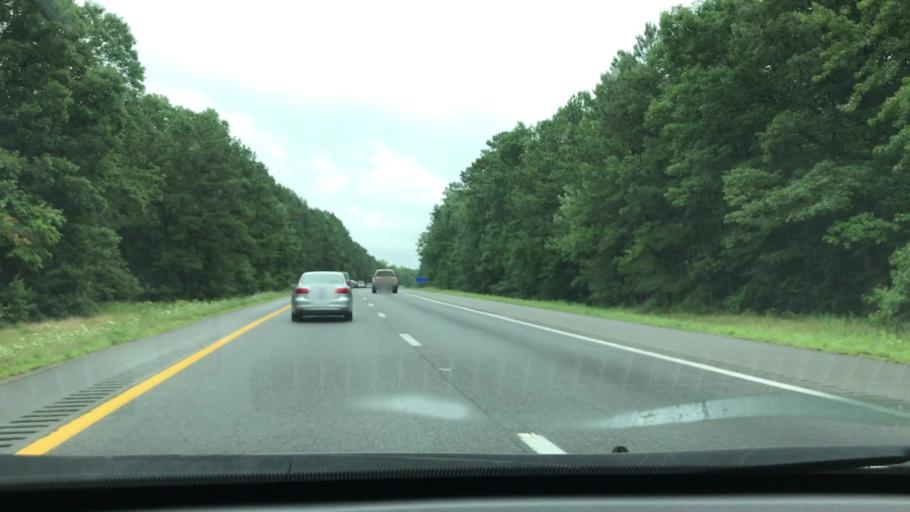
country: US
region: Virginia
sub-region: City of Emporia
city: Emporia
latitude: 36.7582
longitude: -77.5020
